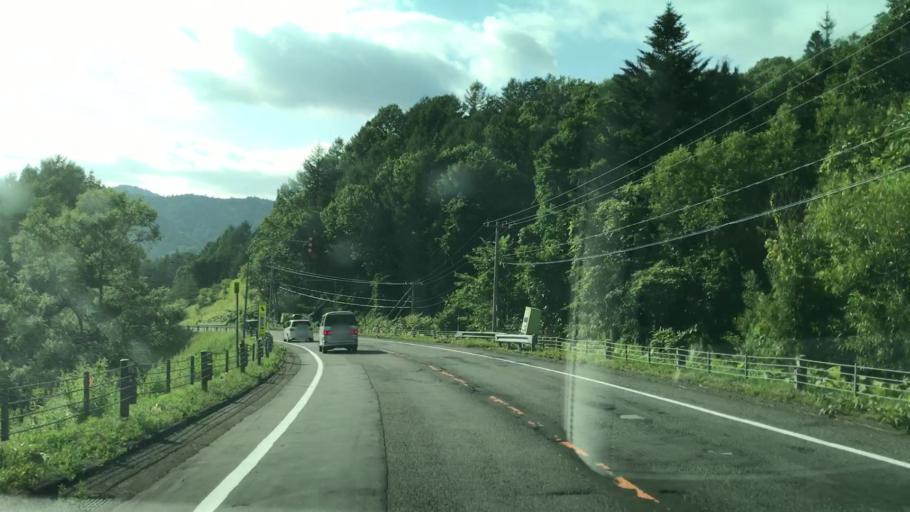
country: JP
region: Hokkaido
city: Shimo-furano
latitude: 42.8904
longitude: 142.1961
